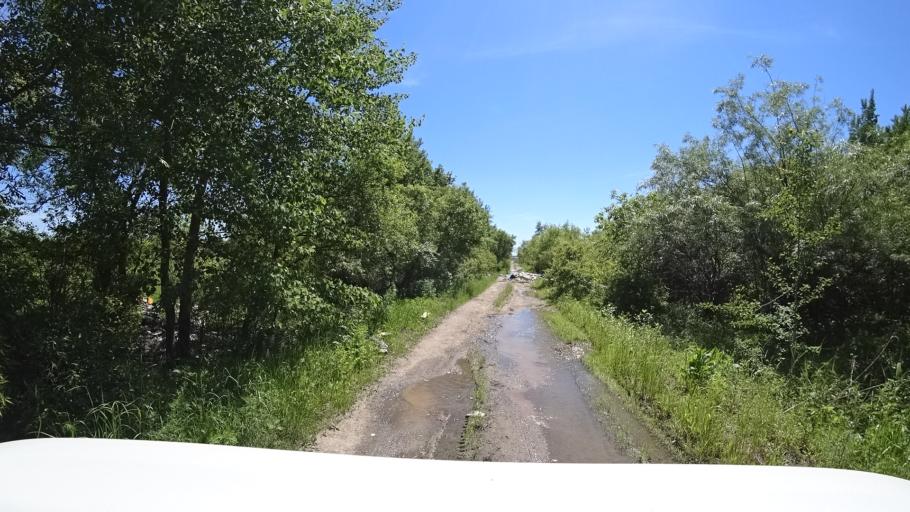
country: RU
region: Khabarovsk Krai
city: Topolevo
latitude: 48.4878
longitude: 135.1773
